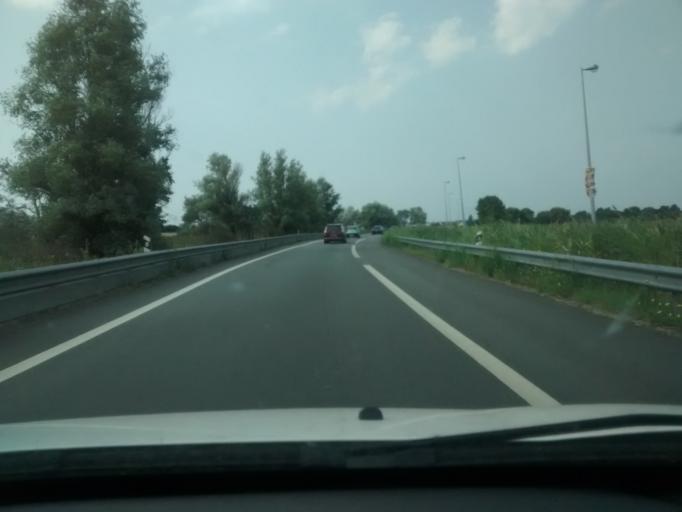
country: FR
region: Pays de la Loire
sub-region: Departement de la Loire-Atlantique
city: Trignac
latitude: 47.3086
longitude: -2.2042
